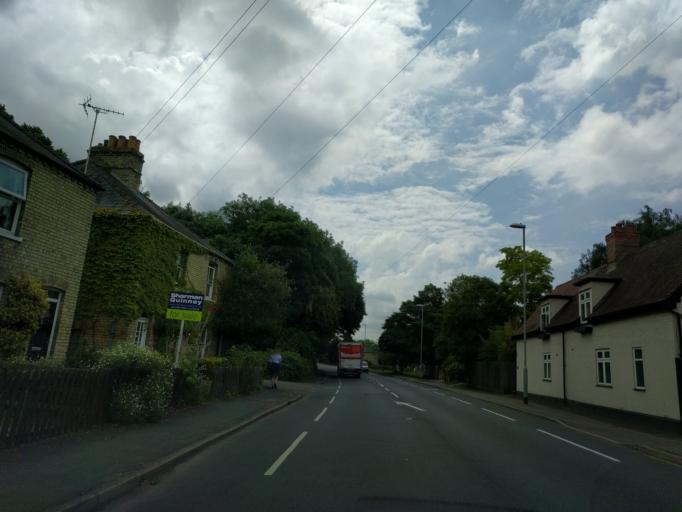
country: GB
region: England
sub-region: Cambridgeshire
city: Histon
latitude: 52.2494
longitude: 0.1088
